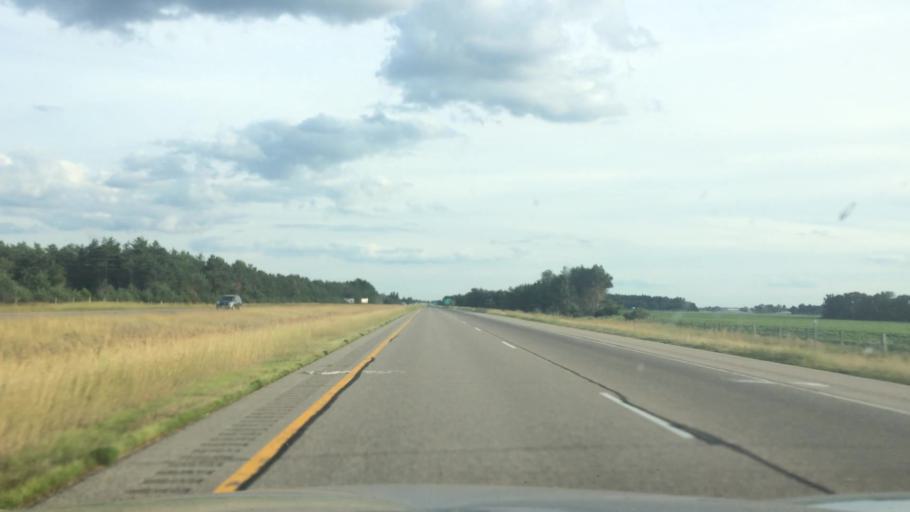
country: US
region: Wisconsin
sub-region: Portage County
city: Plover
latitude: 44.2404
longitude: -89.5244
